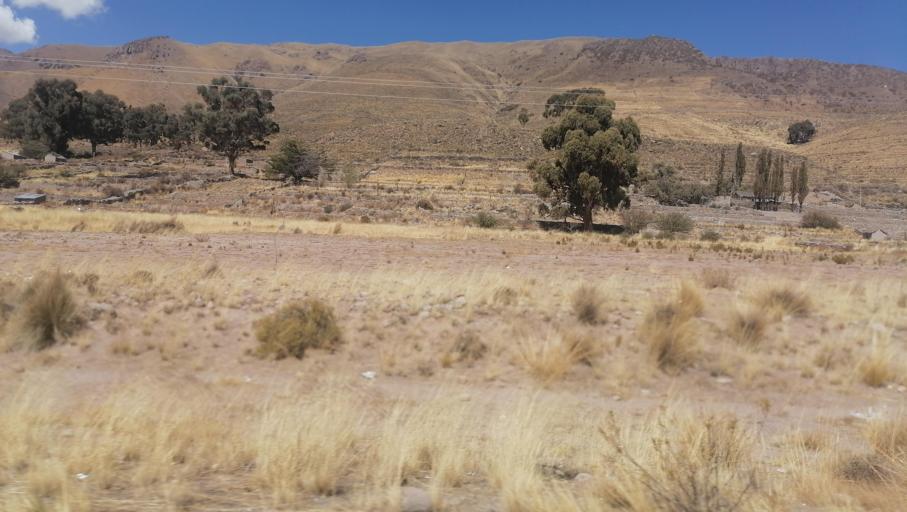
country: BO
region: Oruro
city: Challapata
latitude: -18.9936
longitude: -66.7781
